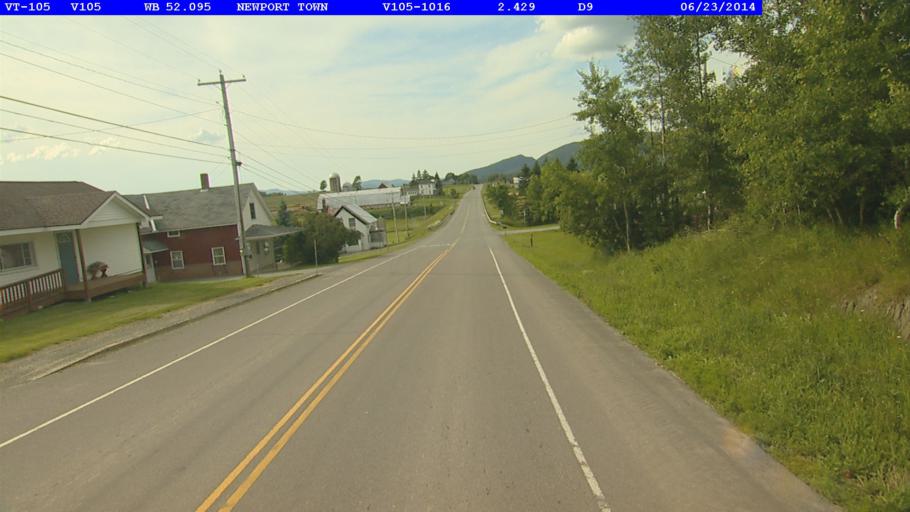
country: US
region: Vermont
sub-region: Orleans County
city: Newport
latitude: 44.9525
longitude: -72.3077
